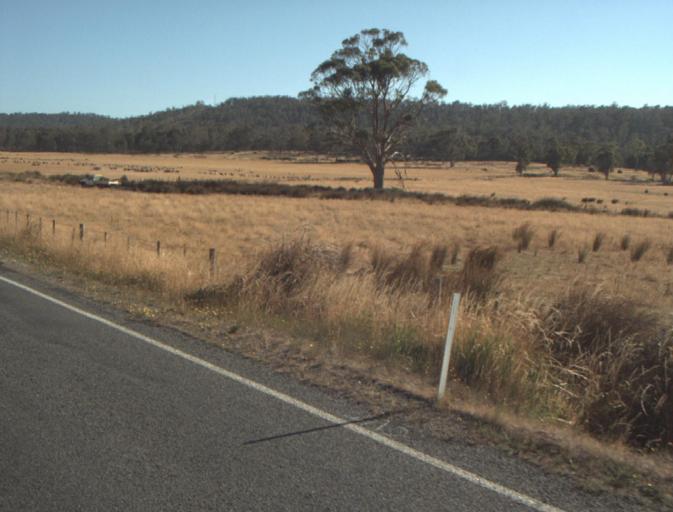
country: AU
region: Tasmania
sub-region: Launceston
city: Newstead
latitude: -41.4405
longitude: 147.2548
